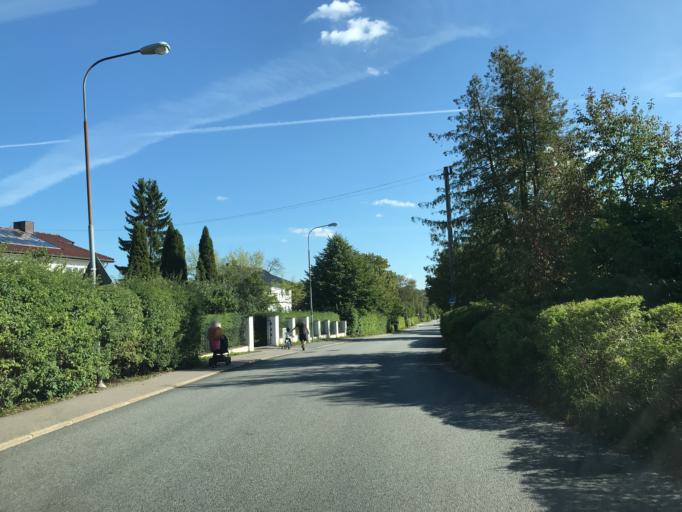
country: SE
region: Stockholm
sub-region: Sollentuna Kommun
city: Sollentuna
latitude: 59.4162
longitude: 17.9809
